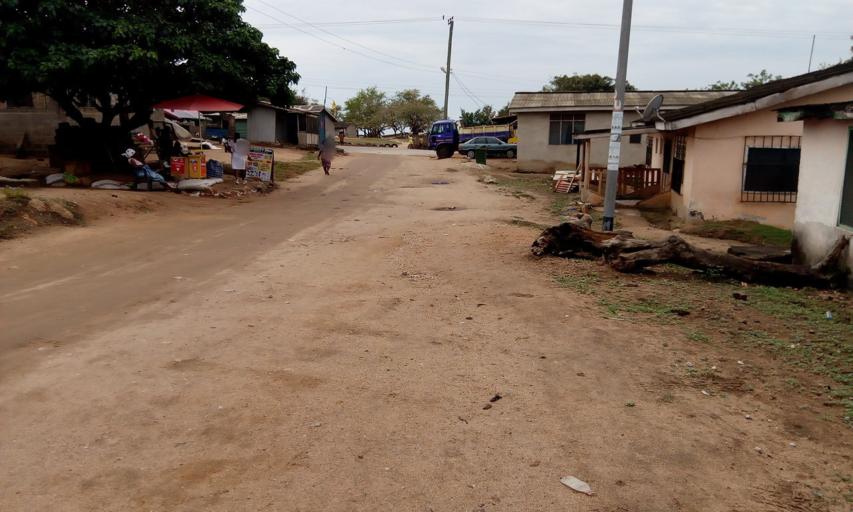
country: GH
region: Central
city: Winneba
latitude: 5.3533
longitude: -0.6180
